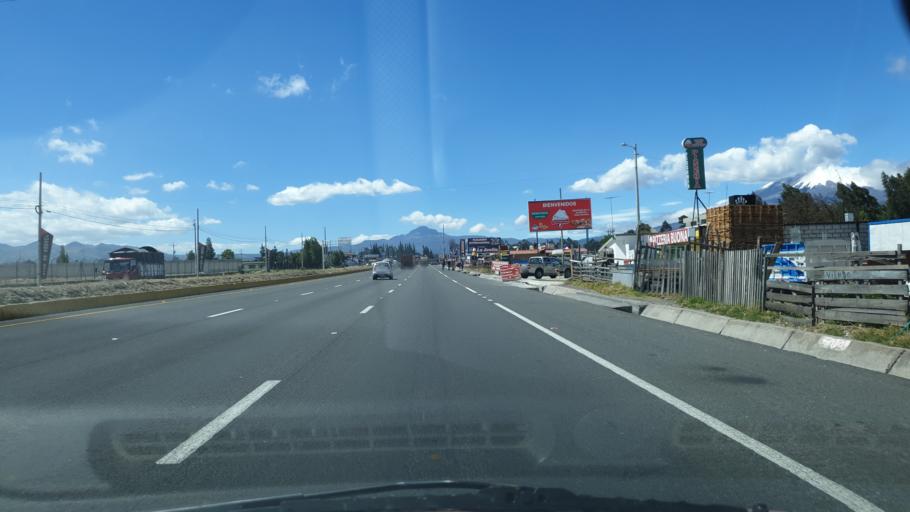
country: EC
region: Cotopaxi
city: Saquisili
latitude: -0.8070
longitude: -78.6224
